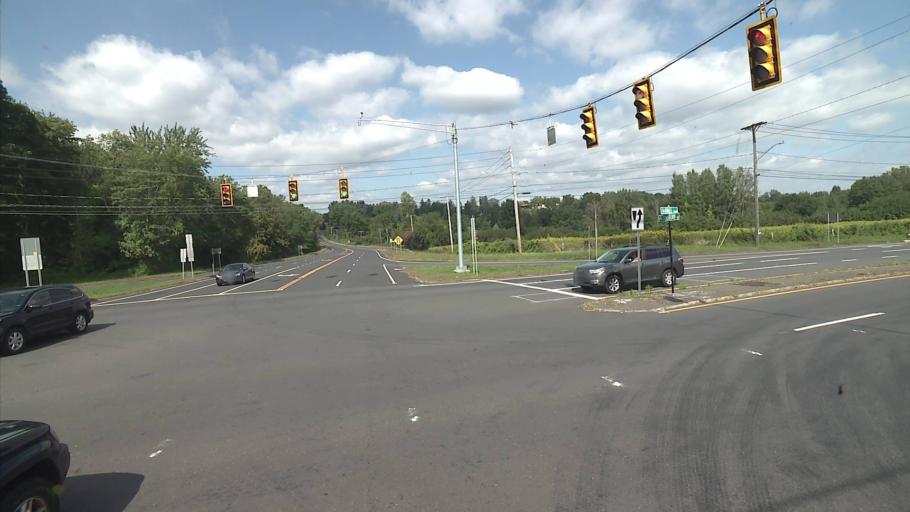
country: US
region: Connecticut
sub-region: Hartford County
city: West Hartford
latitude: 41.8060
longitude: -72.7505
